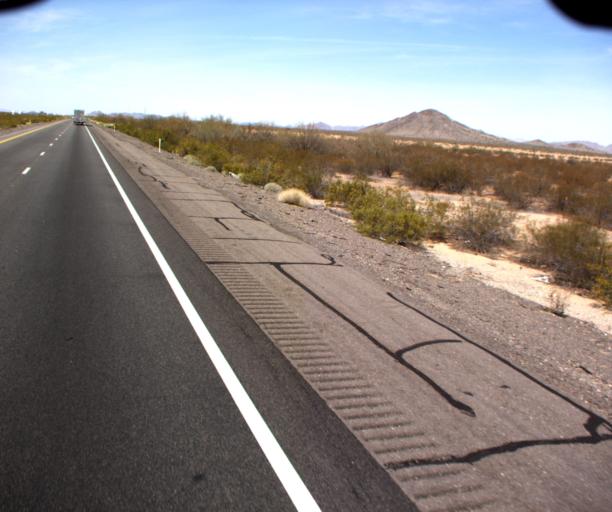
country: US
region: Arizona
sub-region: La Paz County
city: Salome
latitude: 33.5815
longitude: -113.4337
